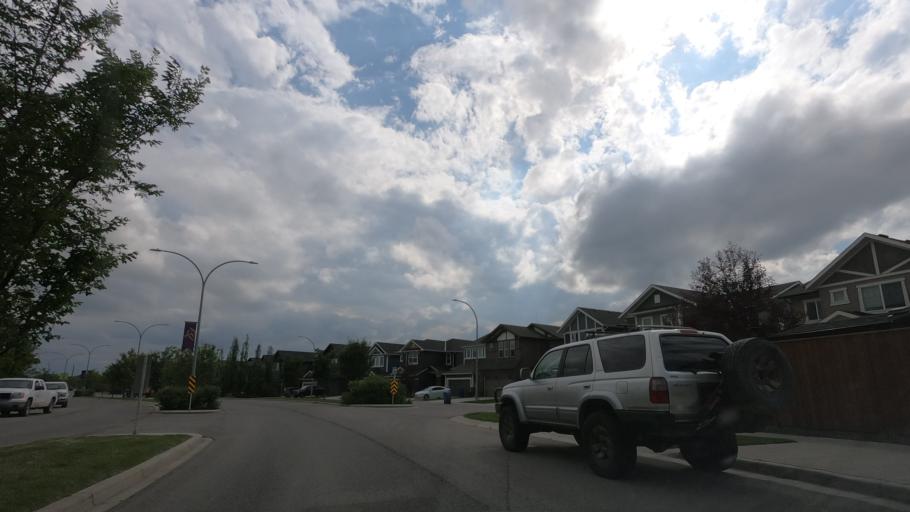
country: CA
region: Alberta
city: Airdrie
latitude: 51.2586
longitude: -113.9917
